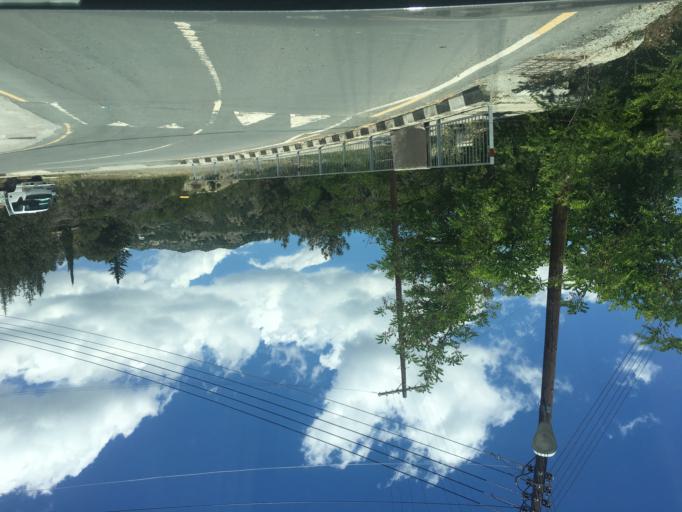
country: CY
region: Limassol
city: Pelendri
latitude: 34.8964
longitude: 33.0184
